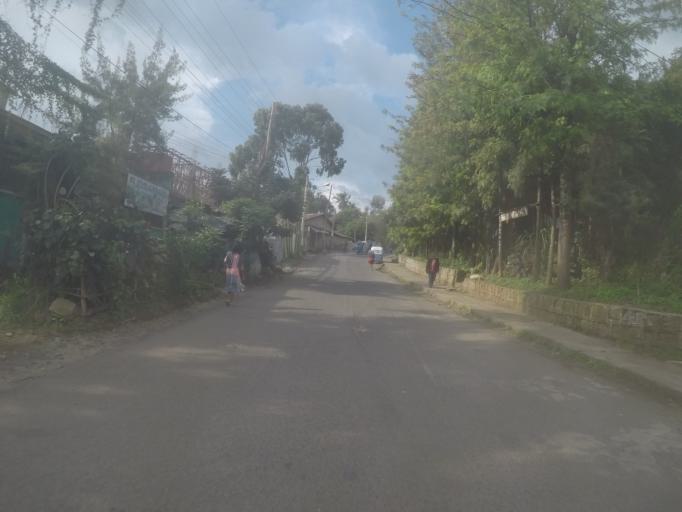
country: ET
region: Amhara
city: Gondar
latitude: 12.6120
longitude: 37.4709
